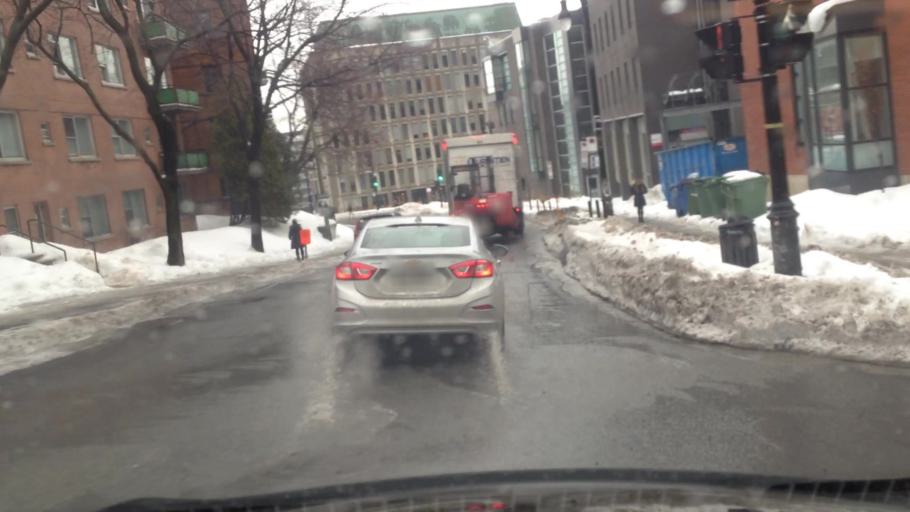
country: CA
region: Quebec
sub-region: Montreal
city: Montreal
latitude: 45.5034
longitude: -73.5795
